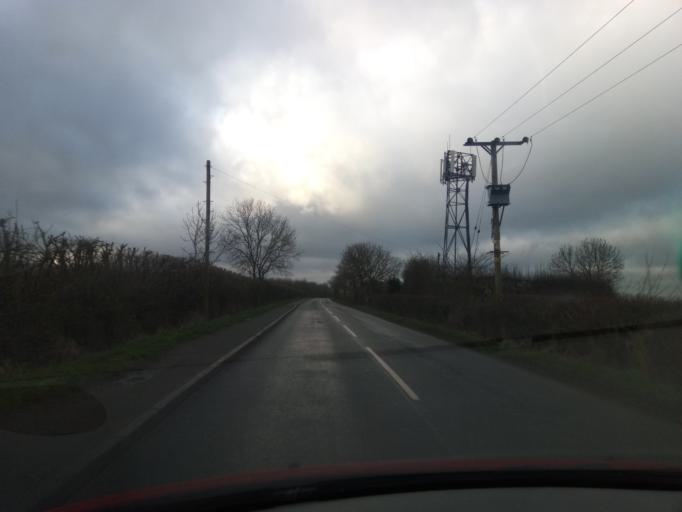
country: GB
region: England
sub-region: Leicestershire
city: Sileby
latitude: 52.7478
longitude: -1.0944
